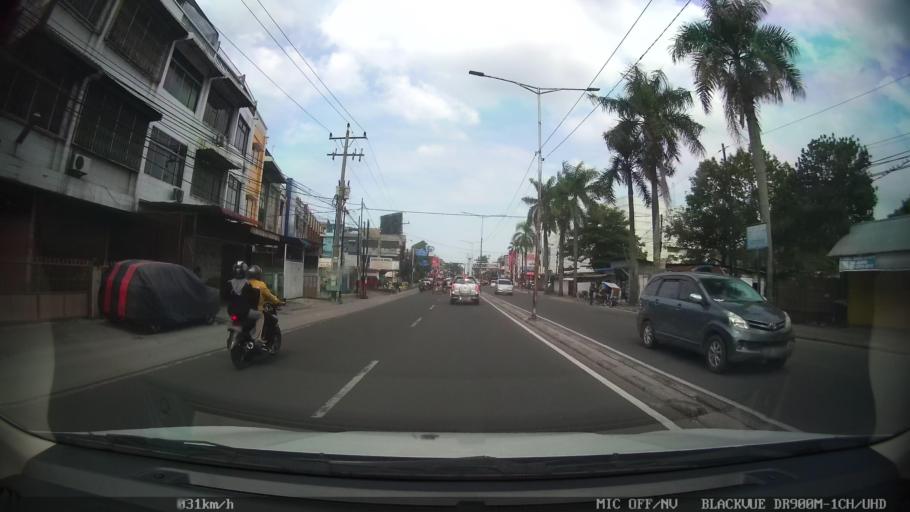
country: ID
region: North Sumatra
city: Medan
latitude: 3.5724
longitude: 98.6841
